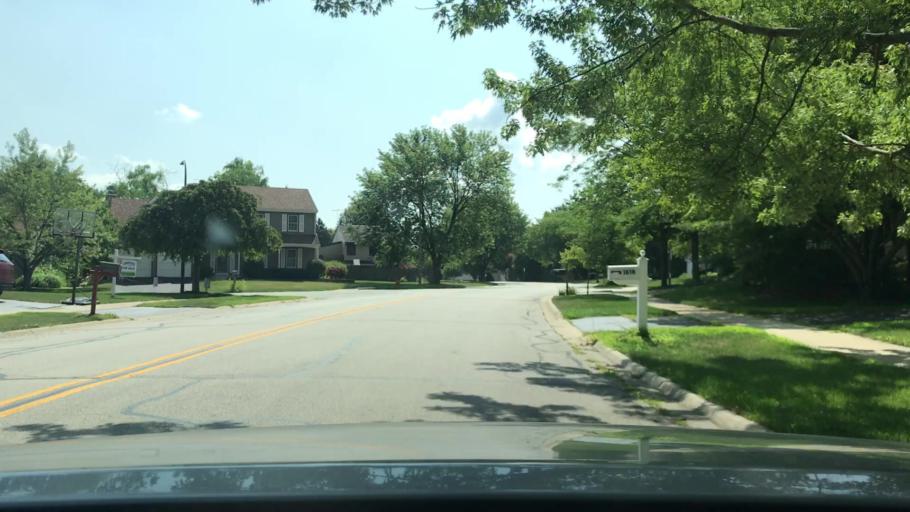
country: US
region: Illinois
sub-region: DuPage County
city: Woodridge
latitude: 41.7437
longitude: -88.0995
